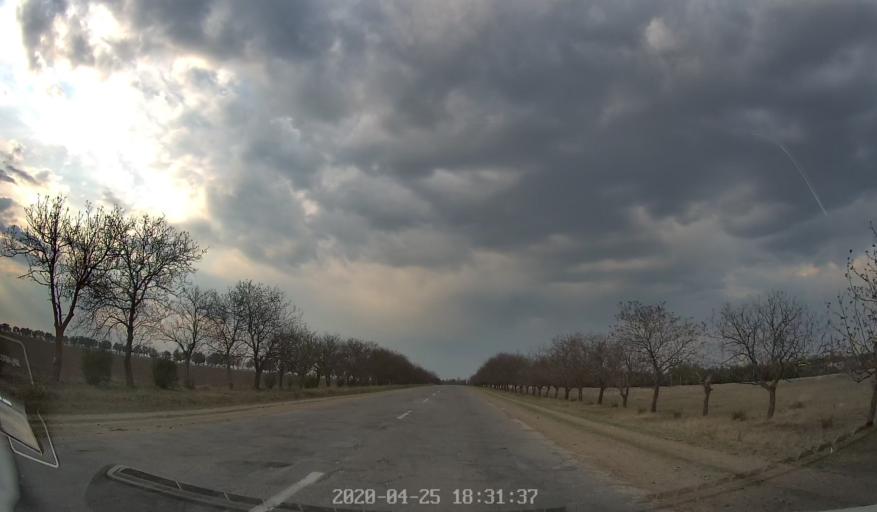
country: MD
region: Criuleni
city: Criuleni
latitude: 47.2197
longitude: 29.1465
